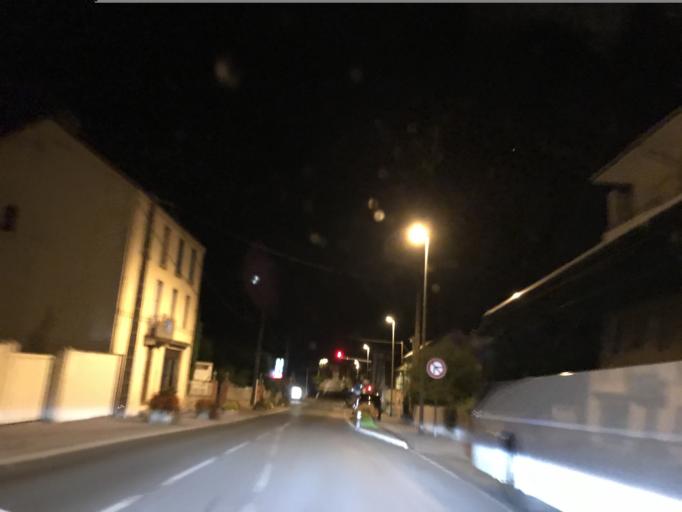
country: FR
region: Auvergne
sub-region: Departement de l'Allier
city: Saint-Yorre
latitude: 46.0668
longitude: 3.4649
